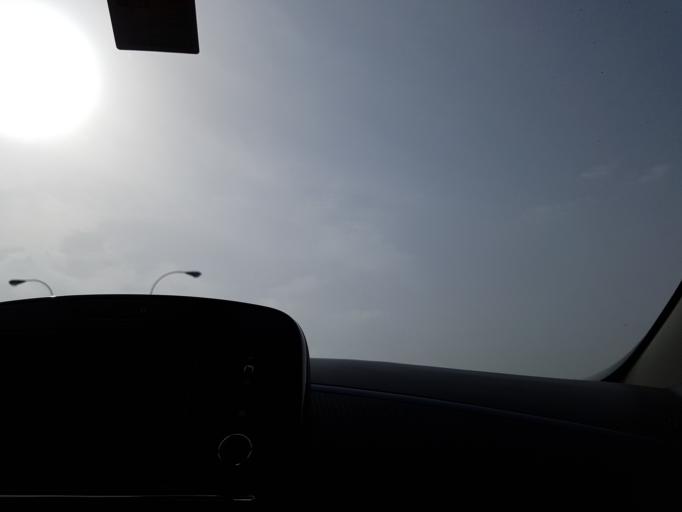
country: OM
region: Al Batinah
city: Al Sohar
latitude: 24.3918
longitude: 56.6941
